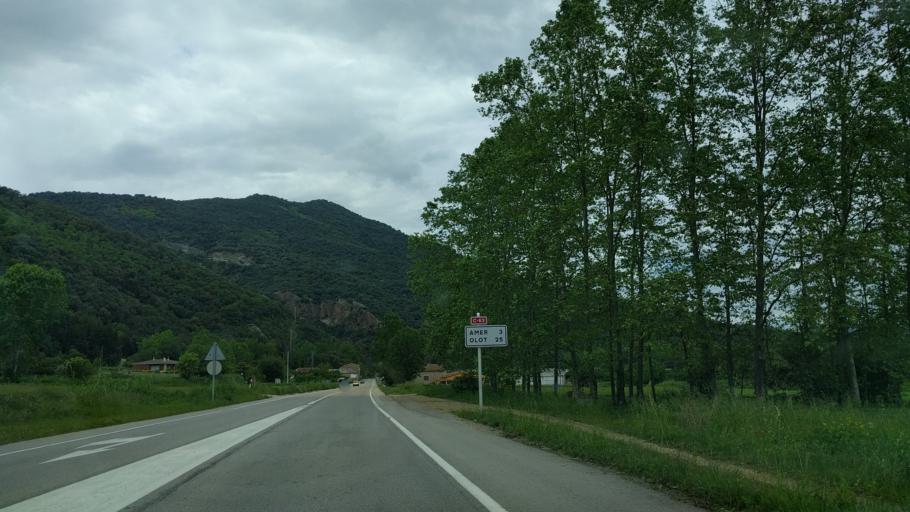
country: ES
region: Catalonia
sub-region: Provincia de Girona
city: la Cellera de Ter
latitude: 41.9811
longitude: 2.6100
